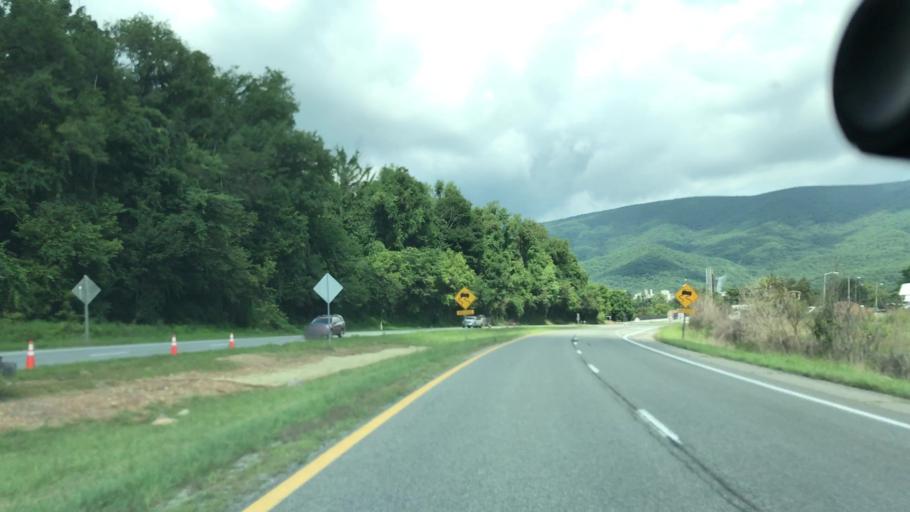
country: US
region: Virginia
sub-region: Giles County
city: Pearisburg
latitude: 37.3361
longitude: -80.7533
